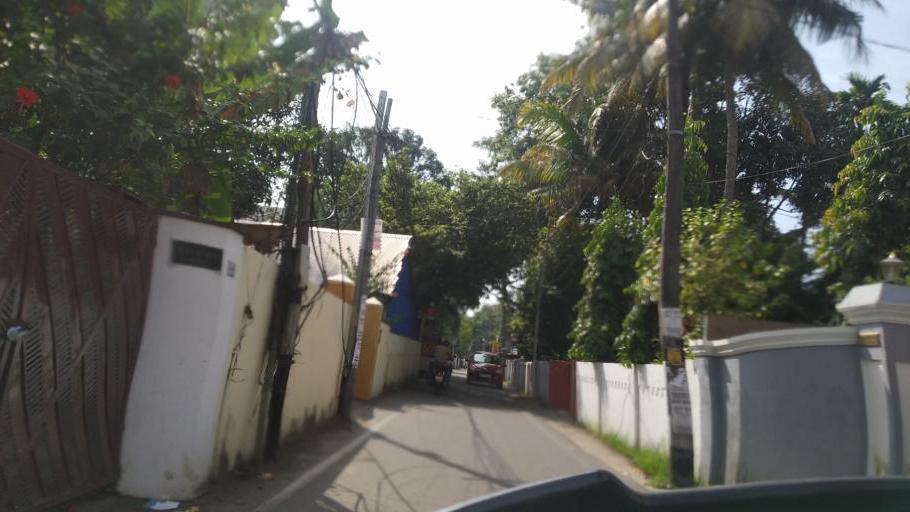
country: IN
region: Kerala
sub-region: Ernakulam
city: Elur
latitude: 10.0065
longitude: 76.2920
